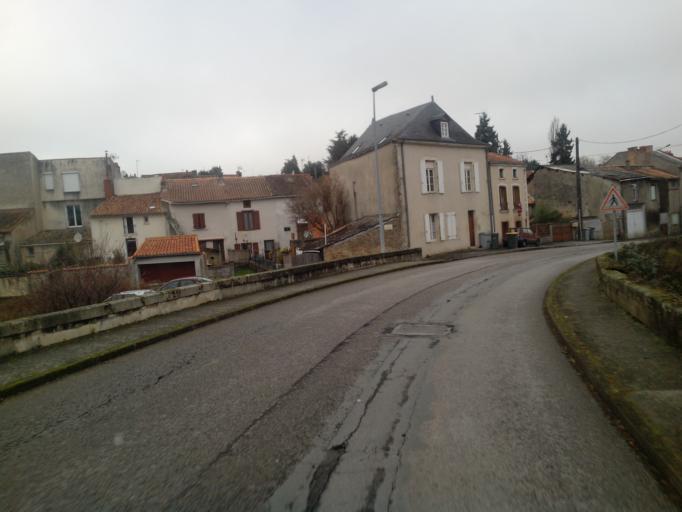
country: FR
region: Poitou-Charentes
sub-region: Departement des Deux-Sevres
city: Parthenay
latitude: 46.6530
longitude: -0.2478
